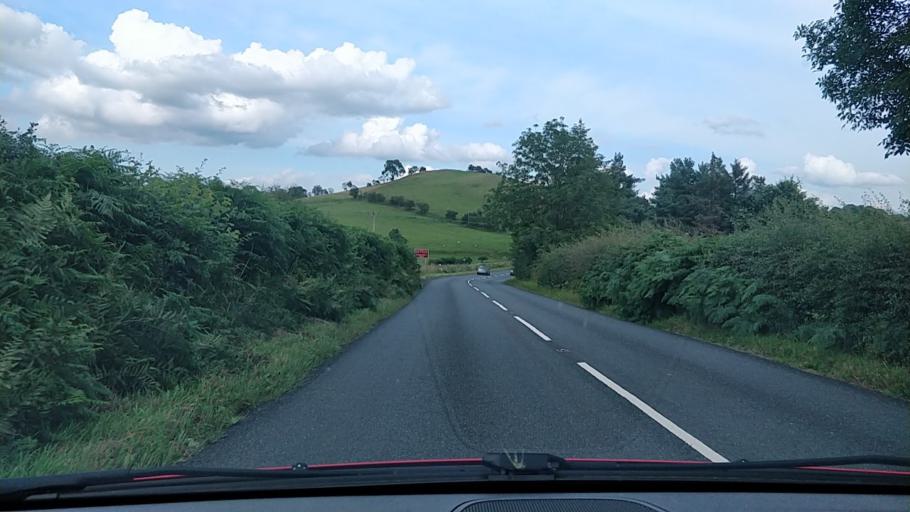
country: GB
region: Wales
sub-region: Denbighshire
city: Corwen
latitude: 52.9968
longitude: -3.3688
